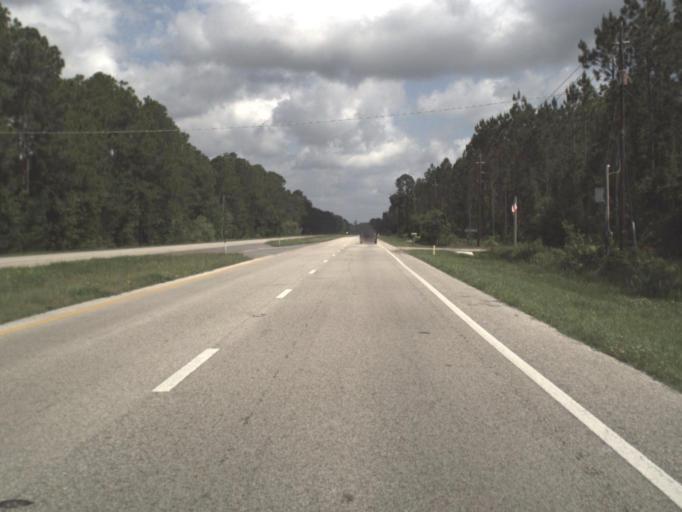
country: US
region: Florida
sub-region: Saint Johns County
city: Butler Beach
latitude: 29.7091
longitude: -81.3006
